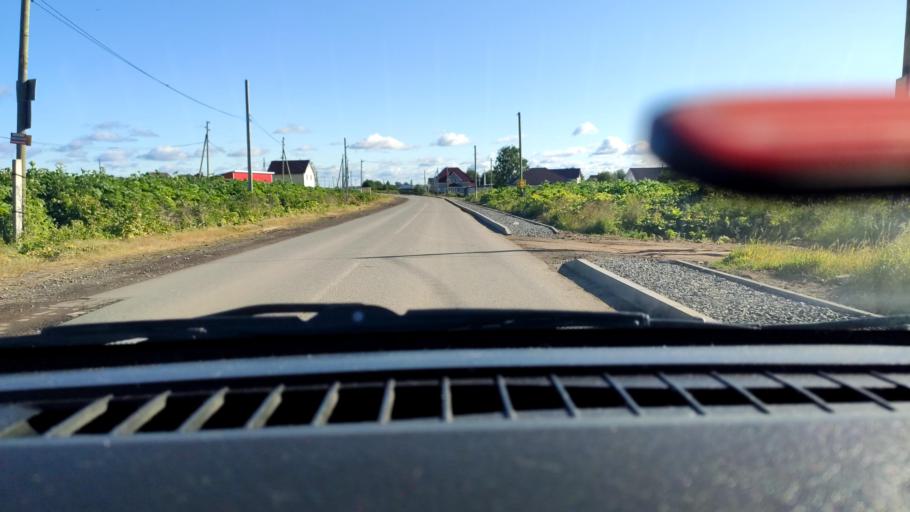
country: RU
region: Perm
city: Kultayevo
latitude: 57.8630
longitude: 55.9145
